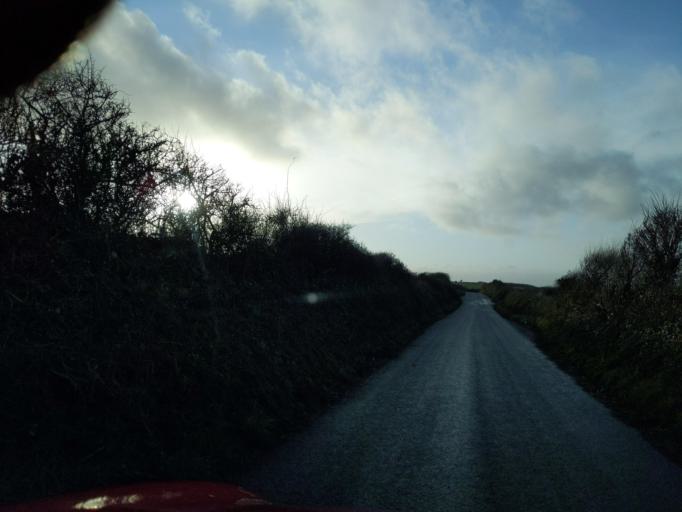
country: GB
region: England
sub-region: Cornwall
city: Fowey
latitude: 50.3300
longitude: -4.6155
